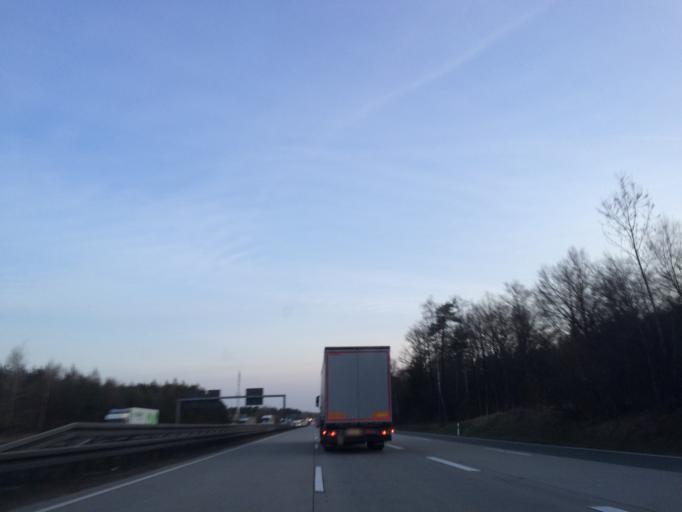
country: DE
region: Thuringia
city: Hermsdorf
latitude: 50.8665
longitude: 11.8513
